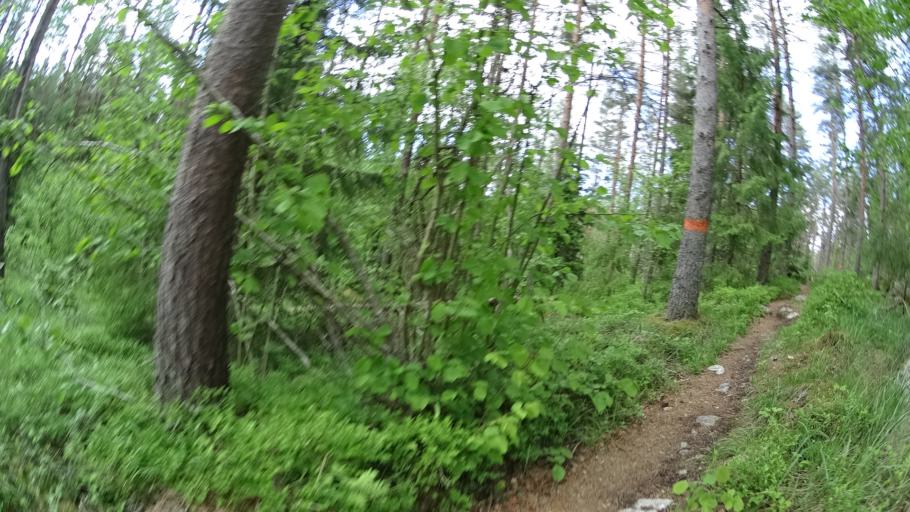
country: FI
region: Uusimaa
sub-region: Raaseporin
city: Pohja
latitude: 60.1437
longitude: 23.5371
